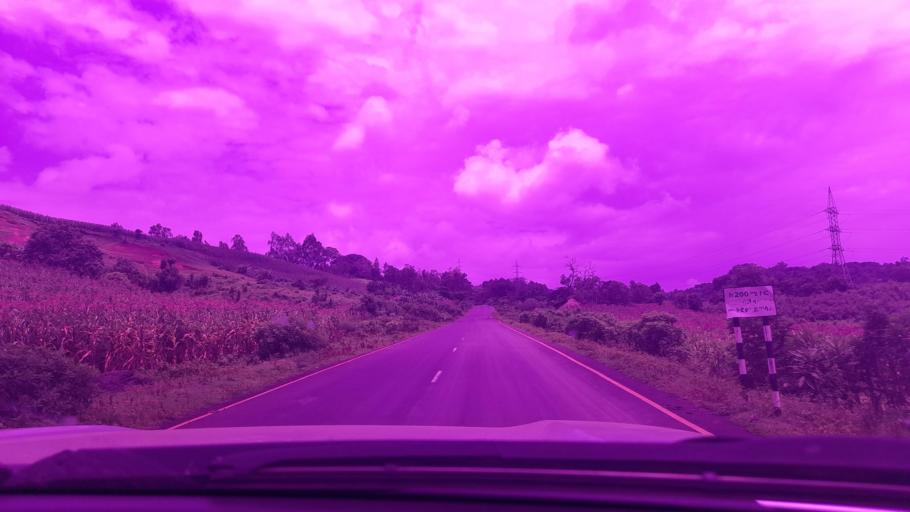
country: ET
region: Oromiya
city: Metu
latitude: 8.3278
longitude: 35.7577
